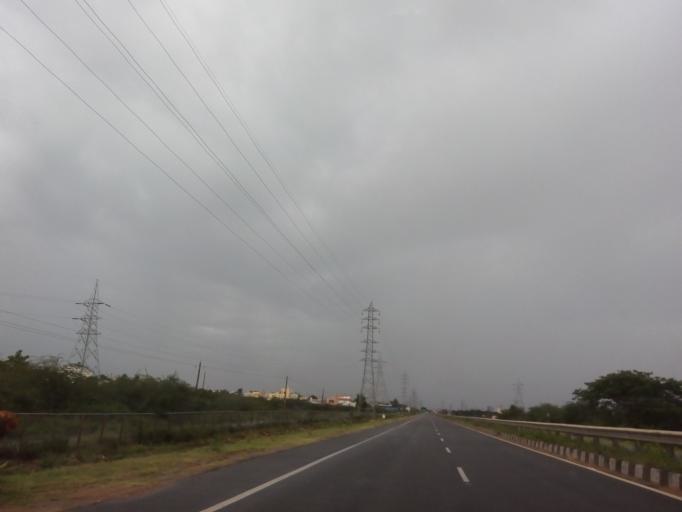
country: IN
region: Karnataka
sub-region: Davanagere
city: Harihar
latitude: 14.4370
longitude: 75.9091
